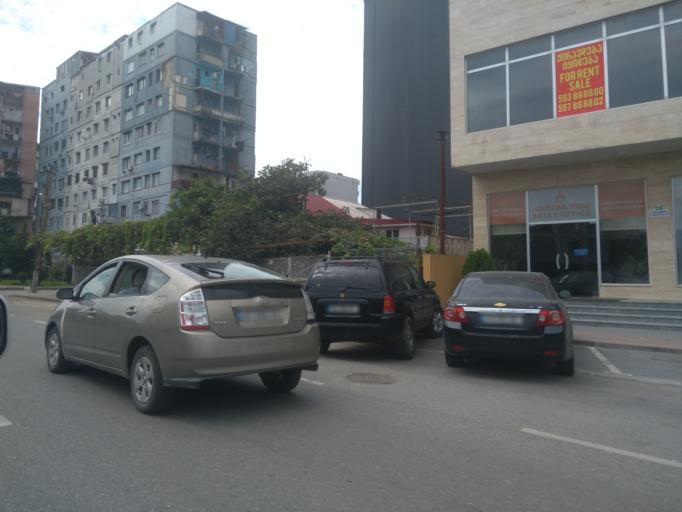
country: GE
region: Ajaria
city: Batumi
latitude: 41.6363
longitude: 41.6323
